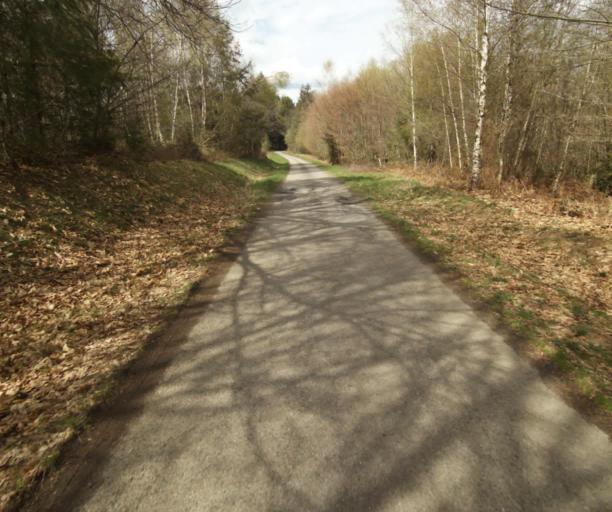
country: FR
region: Limousin
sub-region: Departement de la Correze
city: Argentat
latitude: 45.1929
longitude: 1.9111
